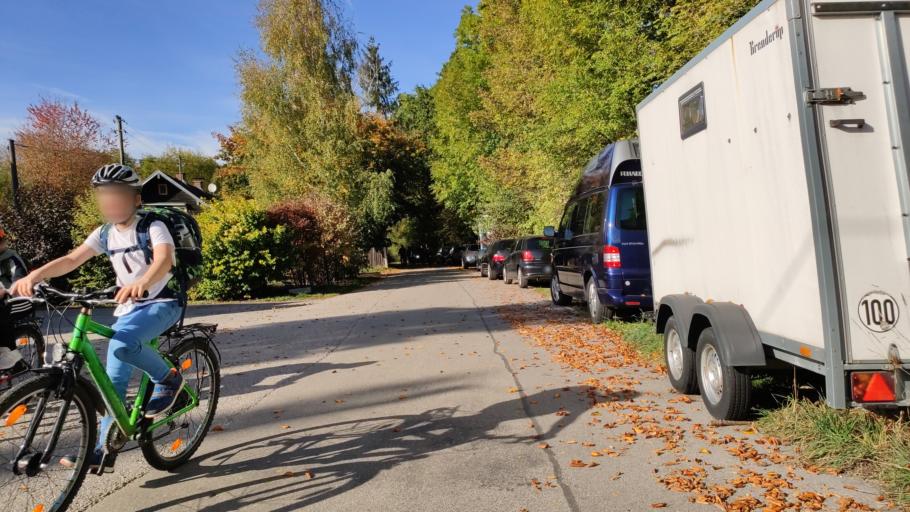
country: DE
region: Bavaria
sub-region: Upper Bavaria
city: Pasing
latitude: 48.1302
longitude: 11.4782
